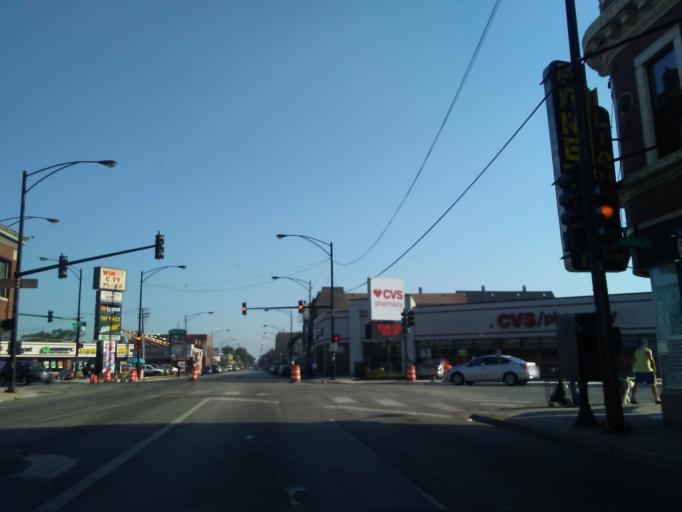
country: US
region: Illinois
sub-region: Cook County
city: Lincolnwood
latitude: 41.9408
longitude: -87.7273
